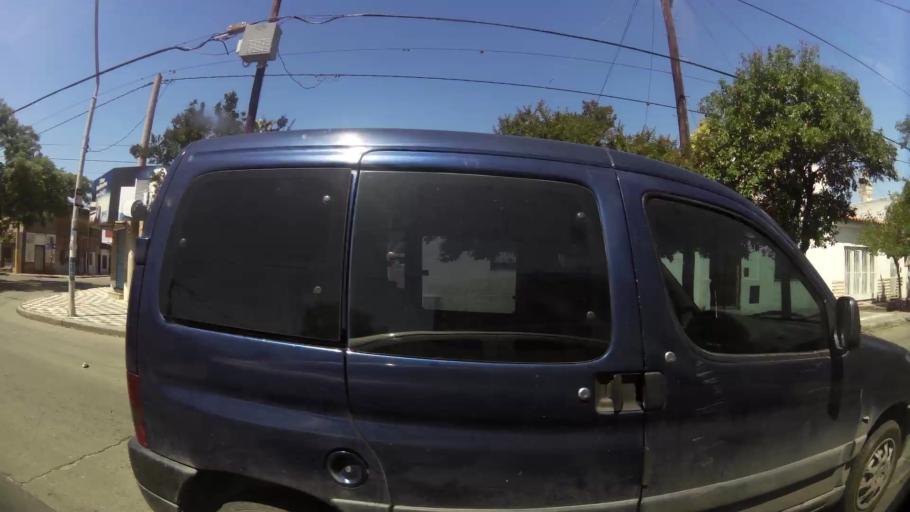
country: AR
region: Cordoba
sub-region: Departamento de Capital
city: Cordoba
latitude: -31.3900
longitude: -64.1961
